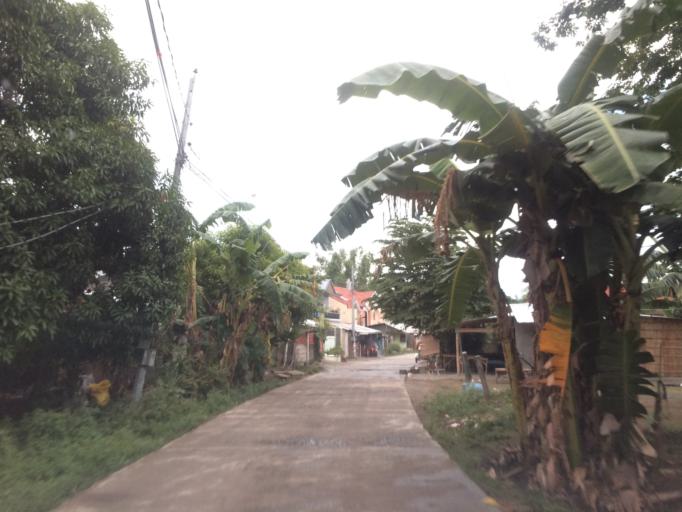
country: PH
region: Ilocos
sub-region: Province of Pangasinan
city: Dumpay
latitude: 15.8795
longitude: 120.3877
